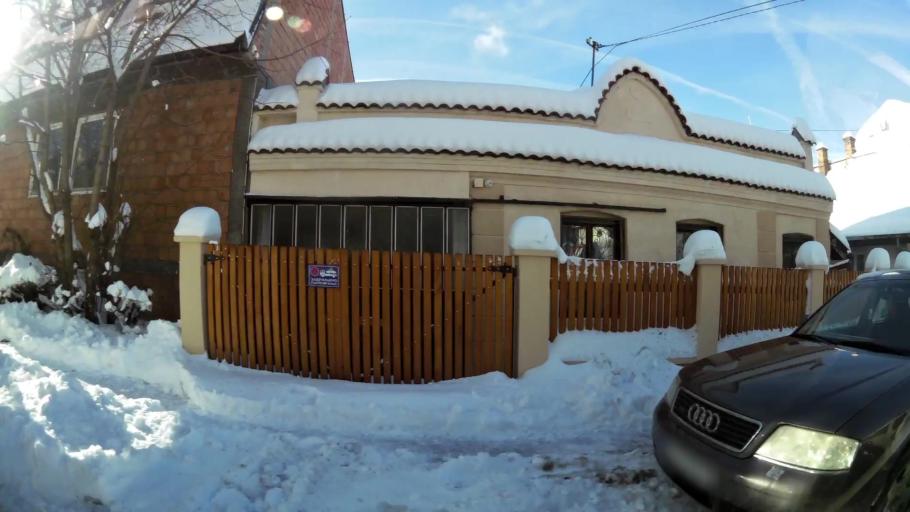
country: RS
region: Central Serbia
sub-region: Belgrade
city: Palilula
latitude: 44.7910
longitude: 20.5112
